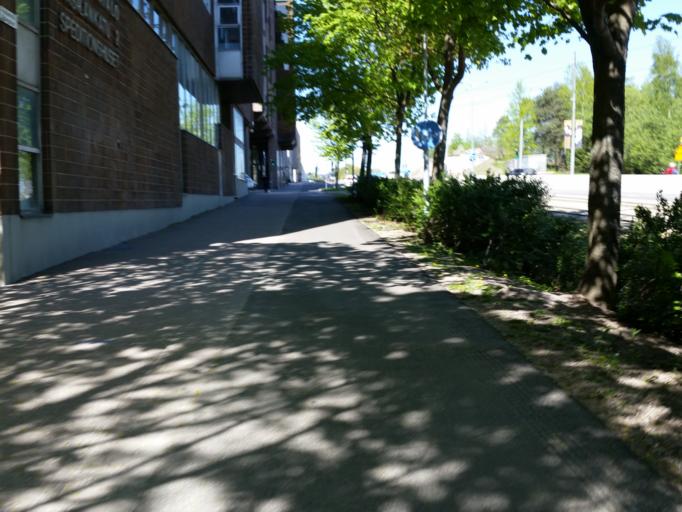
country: FI
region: Uusimaa
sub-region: Helsinki
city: Helsinki
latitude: 60.1955
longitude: 24.9291
